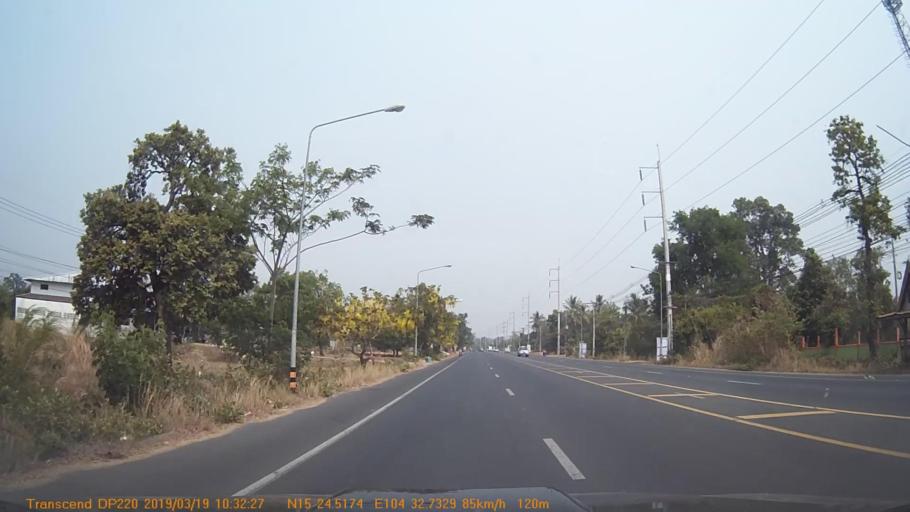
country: TH
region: Changwat Ubon Ratchathani
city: Khueang Nai
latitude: 15.4089
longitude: 104.5455
